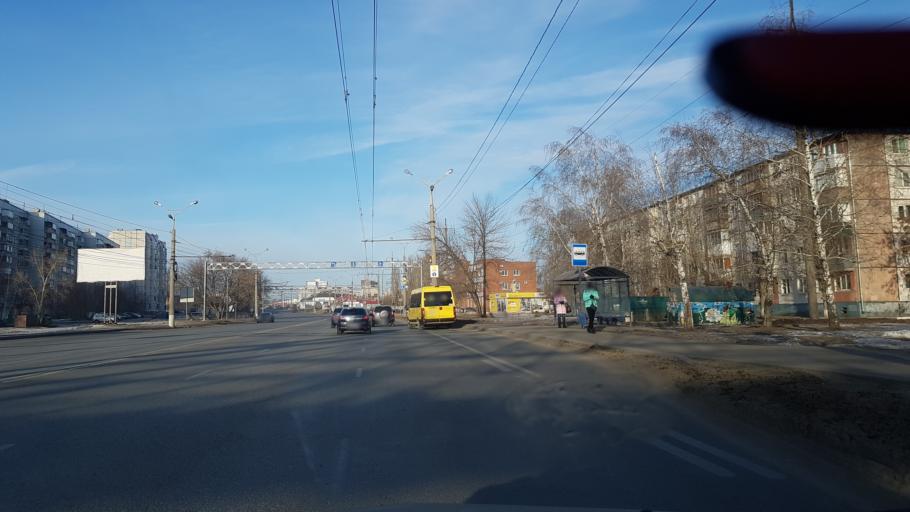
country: RU
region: Samara
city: Tol'yatti
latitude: 53.5302
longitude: 49.3966
